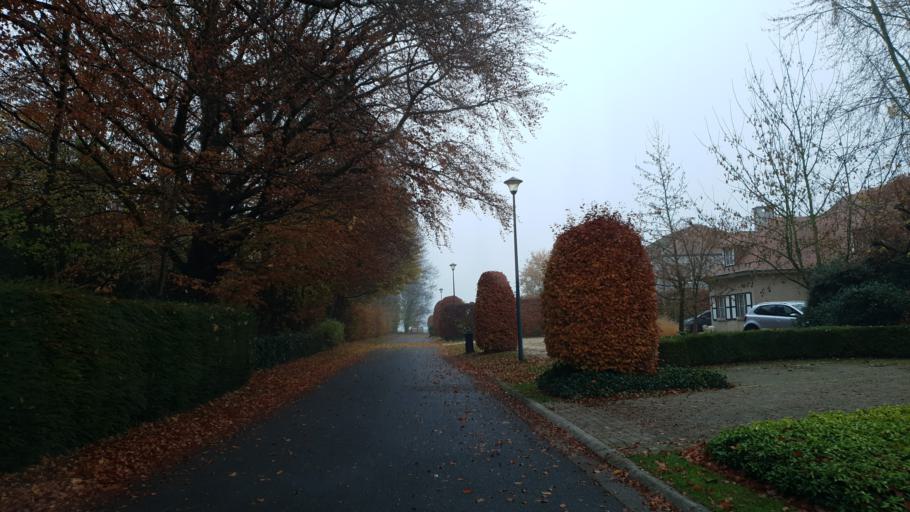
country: BE
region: Flanders
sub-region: Provincie Vlaams-Brabant
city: Kortenberg
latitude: 50.8784
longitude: 4.5146
